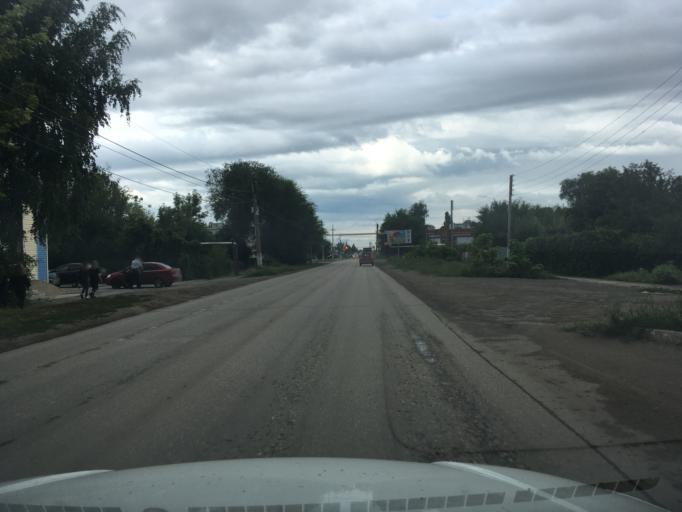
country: RU
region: Samara
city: Bezenchuk
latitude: 52.9824
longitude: 49.4325
